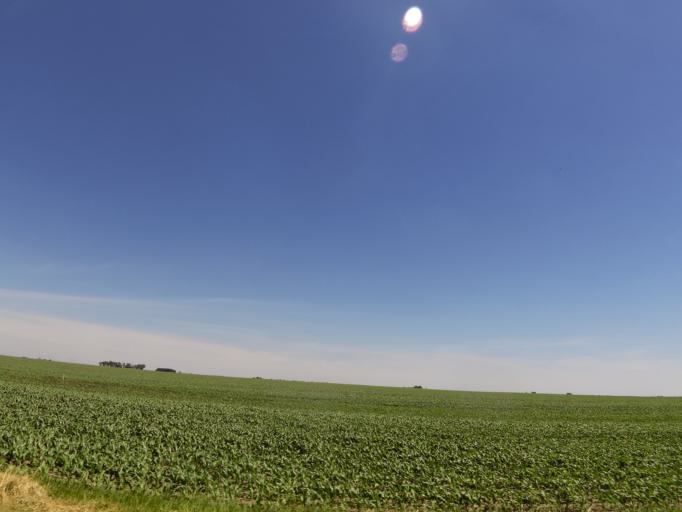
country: US
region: Illinois
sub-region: Iroquois County
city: Watseka
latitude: 40.7364
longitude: -87.8617
